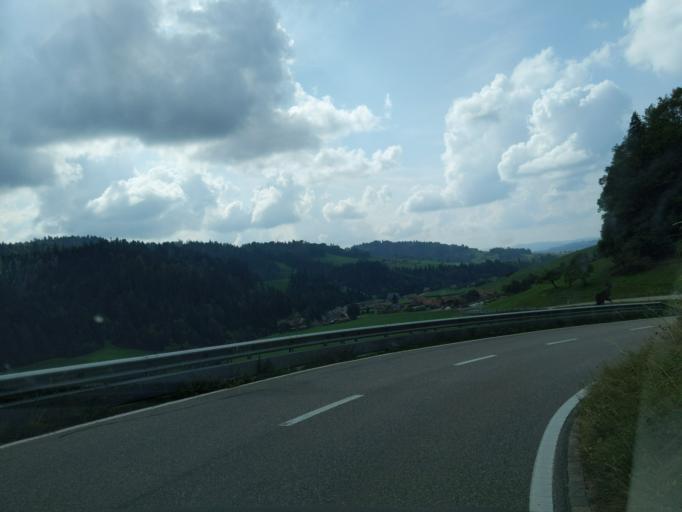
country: CH
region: Bern
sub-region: Oberaargau
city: Wyssachen
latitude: 47.0518
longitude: 7.8308
